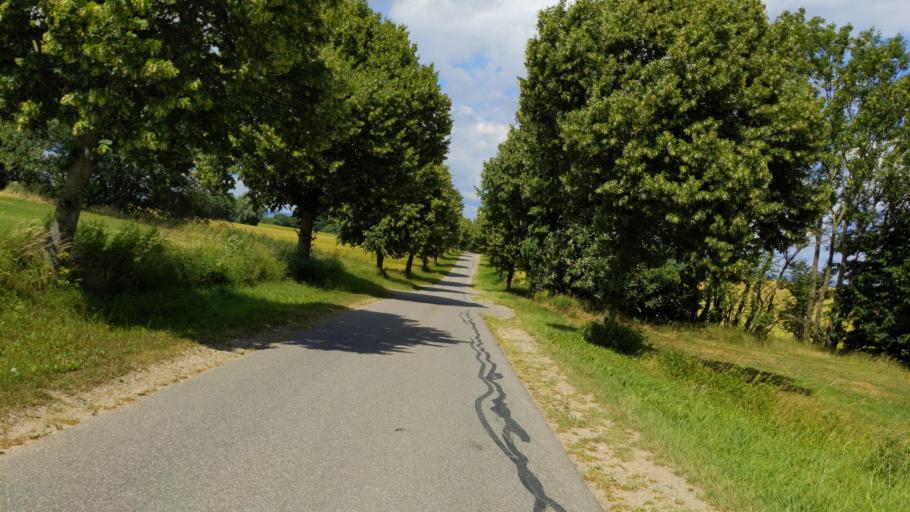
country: DE
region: Mecklenburg-Vorpommern
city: Kalkhorst
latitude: 53.9890
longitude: 11.0795
